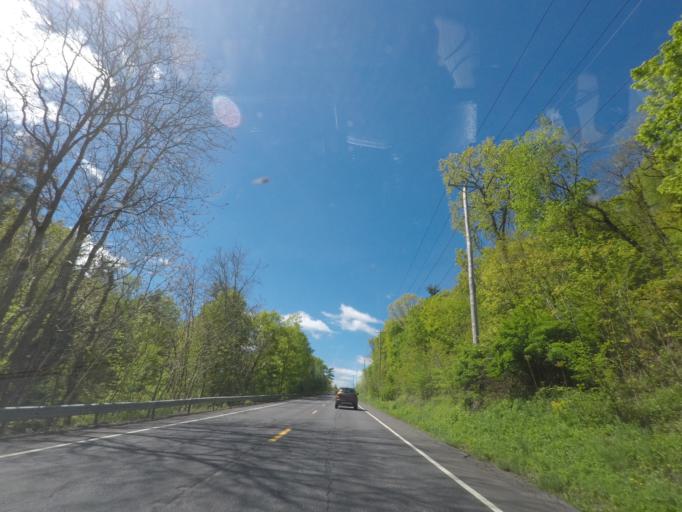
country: US
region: New York
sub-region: Ulster County
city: Lake Katrine
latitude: 42.0166
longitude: -73.9785
